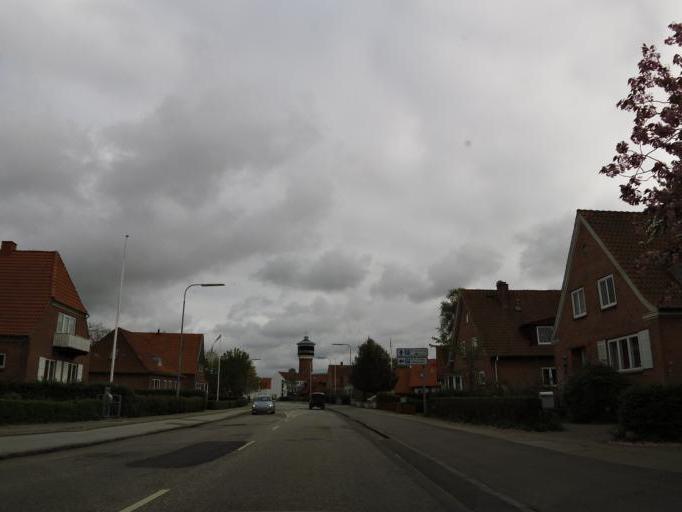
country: DK
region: South Denmark
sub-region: Tonder Kommune
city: Tonder
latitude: 54.9341
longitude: 8.8641
